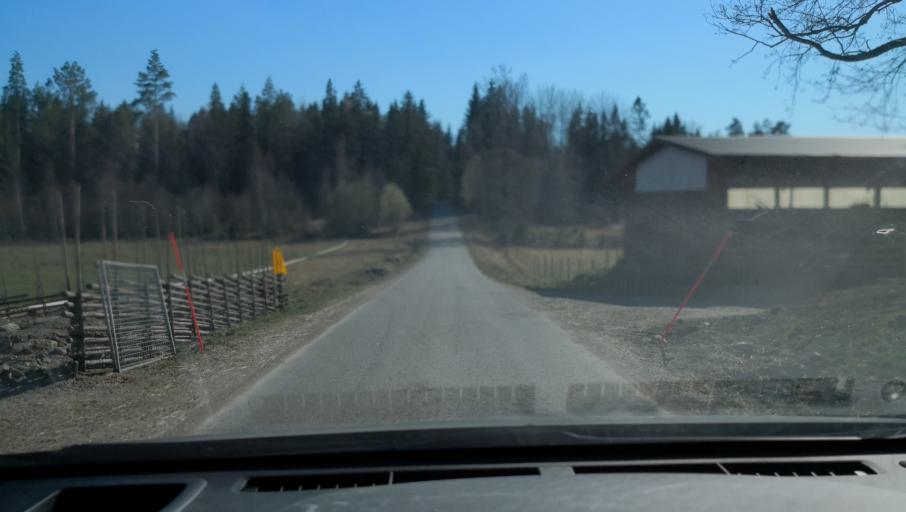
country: SE
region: Dalarna
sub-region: Avesta Kommun
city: Horndal
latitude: 60.0883
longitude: 16.4034
